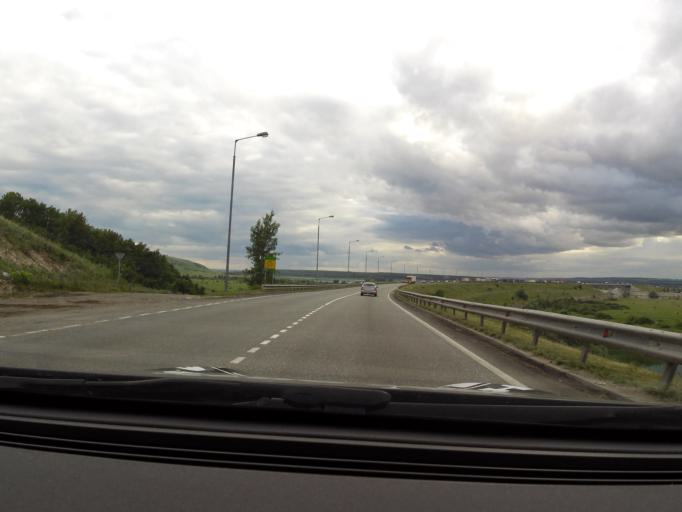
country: RU
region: Tatarstan
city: Sviyazhsk
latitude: 55.7199
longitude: 48.6076
